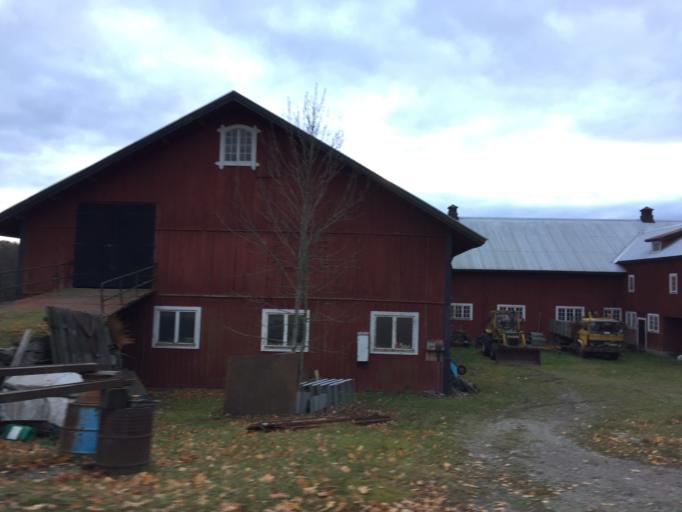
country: SE
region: Stockholm
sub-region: Botkyrka Kommun
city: Eriksberg
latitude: 59.2239
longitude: 17.7980
